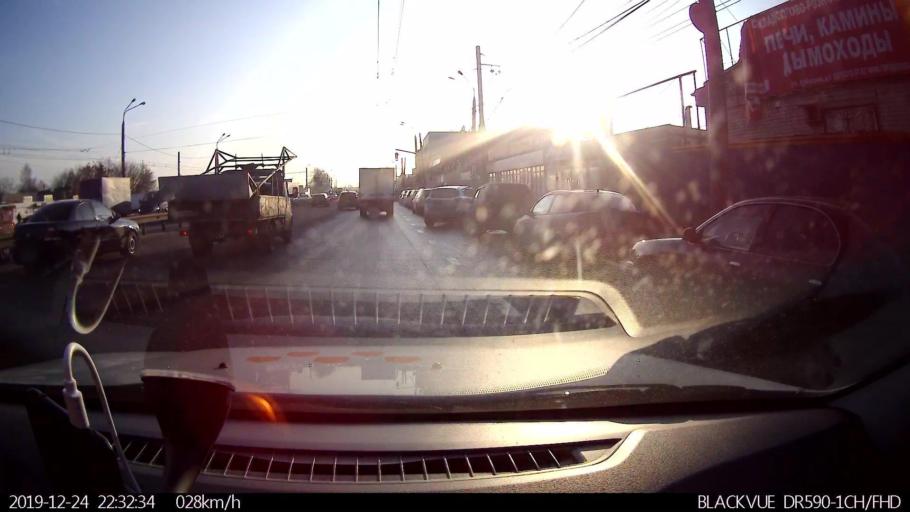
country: RU
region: Nizjnij Novgorod
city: Nizhniy Novgorod
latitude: 56.3054
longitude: 43.8716
